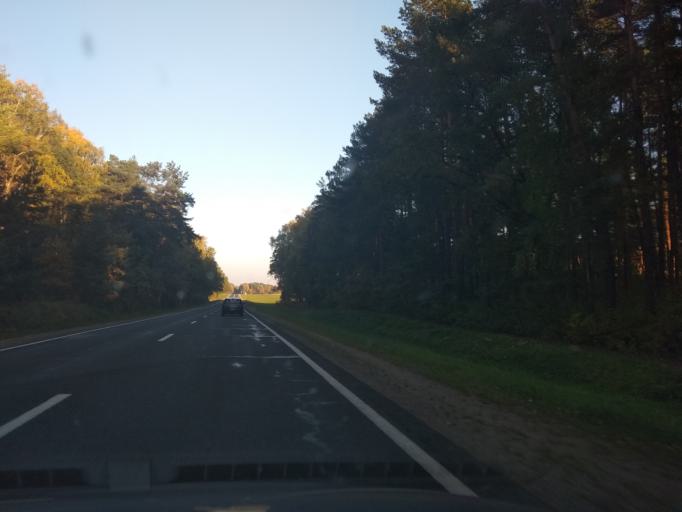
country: BY
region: Grodnenskaya
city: Vawkavysk
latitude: 53.1416
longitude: 24.6331
